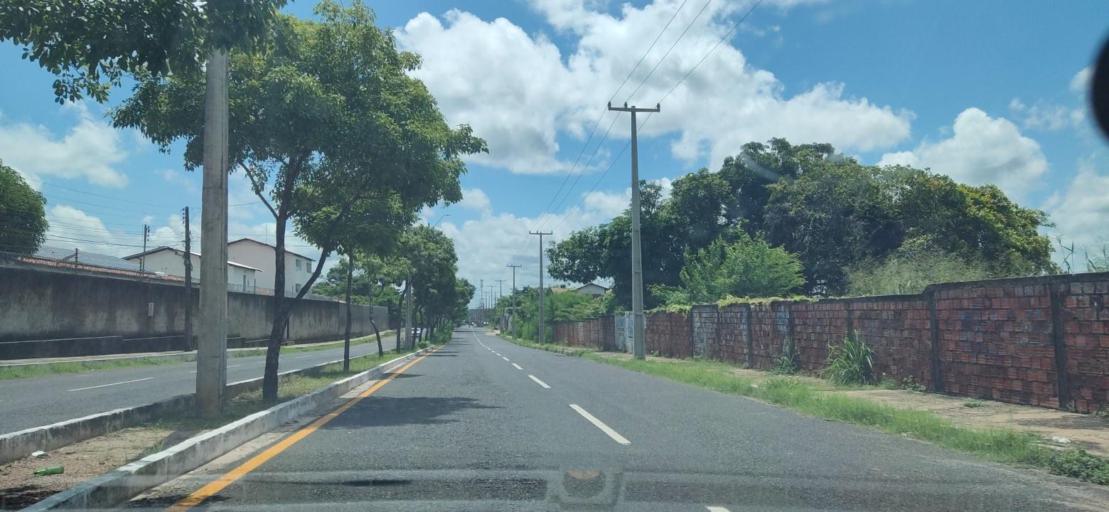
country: BR
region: Piaui
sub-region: Teresina
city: Teresina
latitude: -5.0643
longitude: -42.7586
